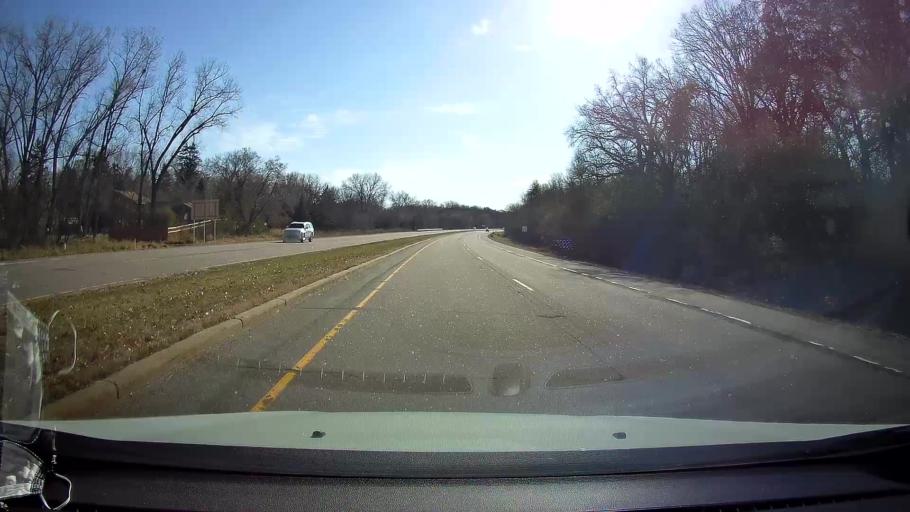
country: US
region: Minnesota
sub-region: Ramsey County
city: Arden Hills
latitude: 45.0444
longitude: -93.1570
